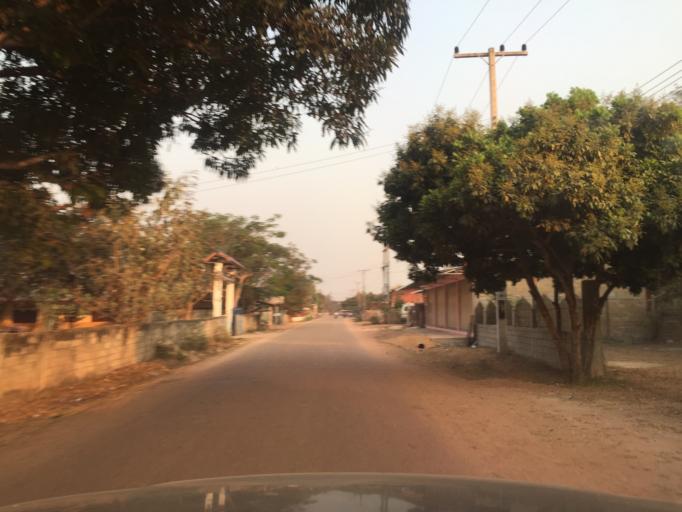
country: LA
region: Vientiane
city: Vientiane
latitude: 18.0618
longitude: 102.5250
